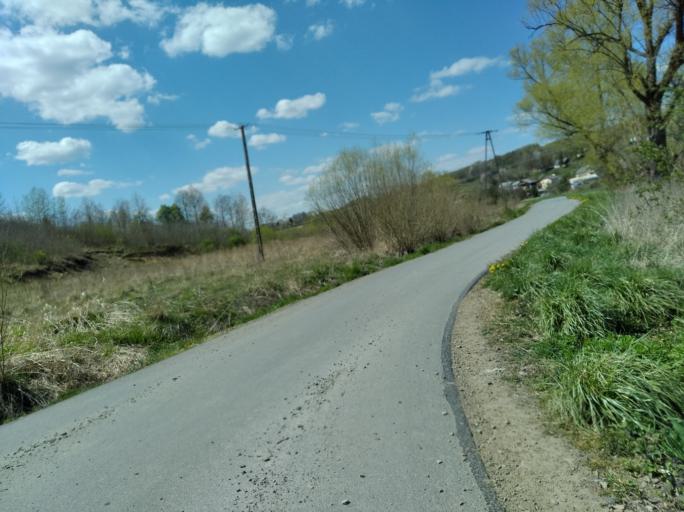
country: PL
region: Subcarpathian Voivodeship
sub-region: Powiat brzozowski
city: Domaradz
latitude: 49.7889
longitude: 21.9778
